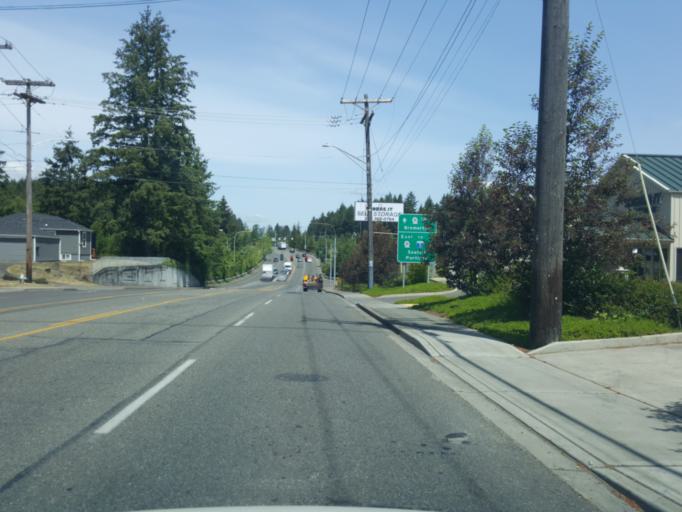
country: US
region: Washington
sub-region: Pierce County
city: Fircrest
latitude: 47.2391
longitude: -122.5049
